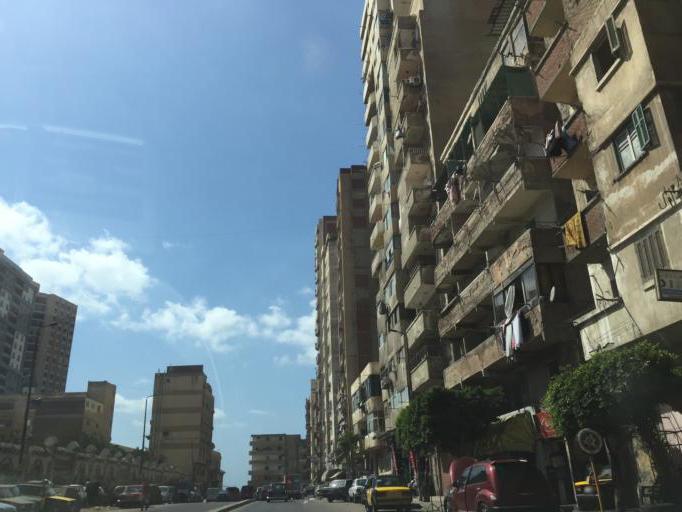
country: EG
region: Alexandria
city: Alexandria
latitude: 31.2608
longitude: 29.9868
